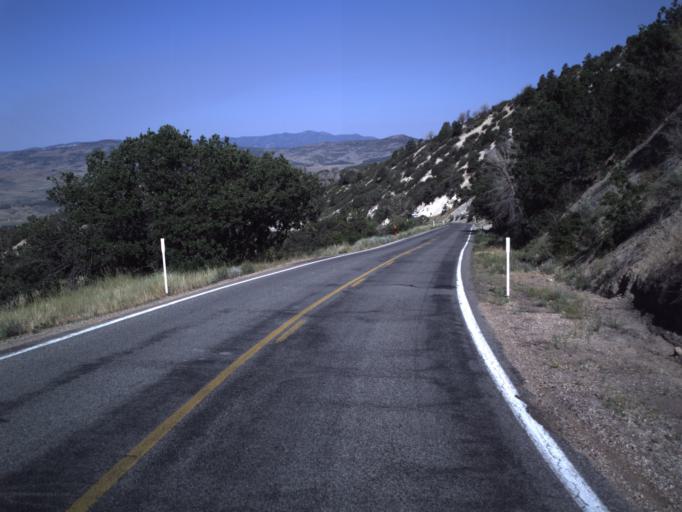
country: US
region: Utah
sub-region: Sanpete County
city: Fairview
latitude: 39.6486
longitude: -111.3966
